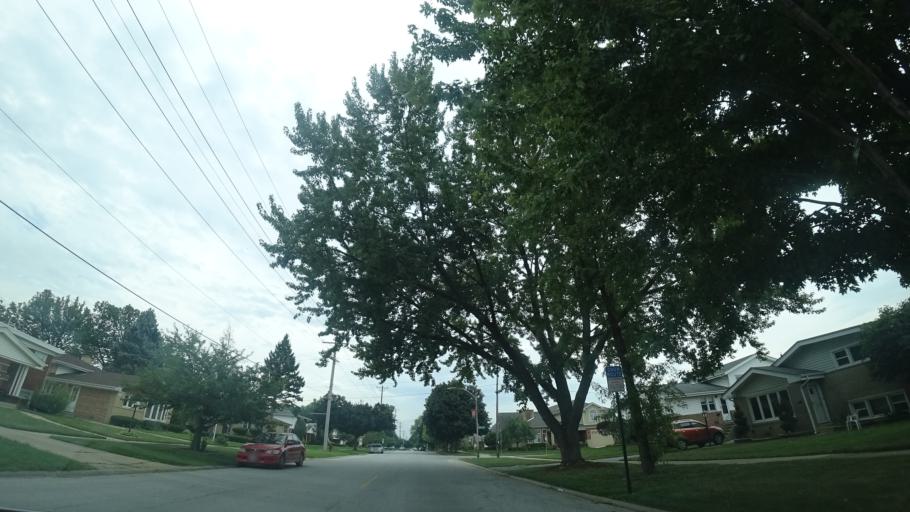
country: US
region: Illinois
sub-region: Cook County
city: Oak Lawn
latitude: 41.7007
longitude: -87.7304
